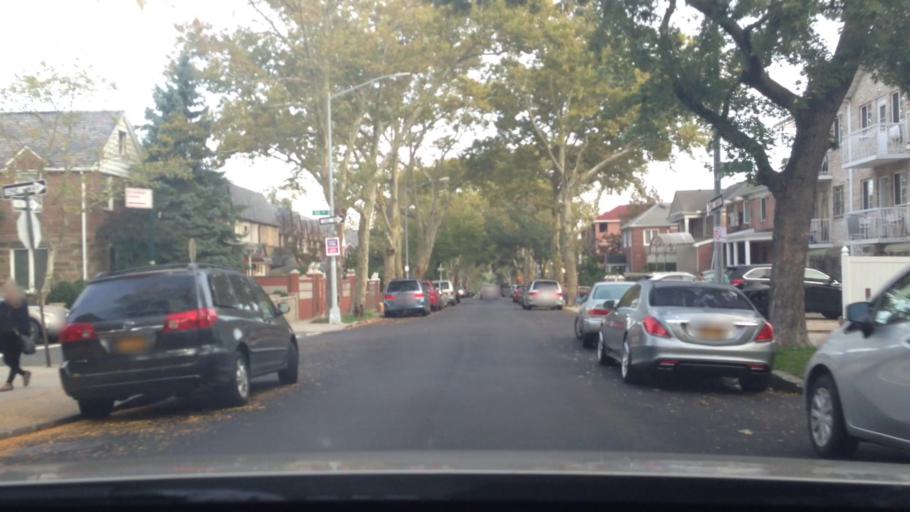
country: US
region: New York
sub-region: Queens County
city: Borough of Queens
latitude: 40.7307
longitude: -73.8459
